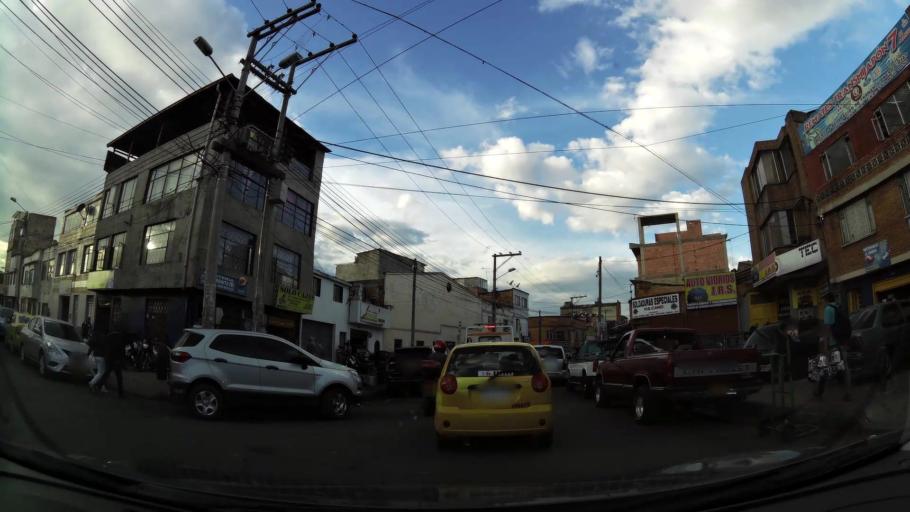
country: CO
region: Bogota D.C.
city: Bogota
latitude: 4.6584
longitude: -74.0749
